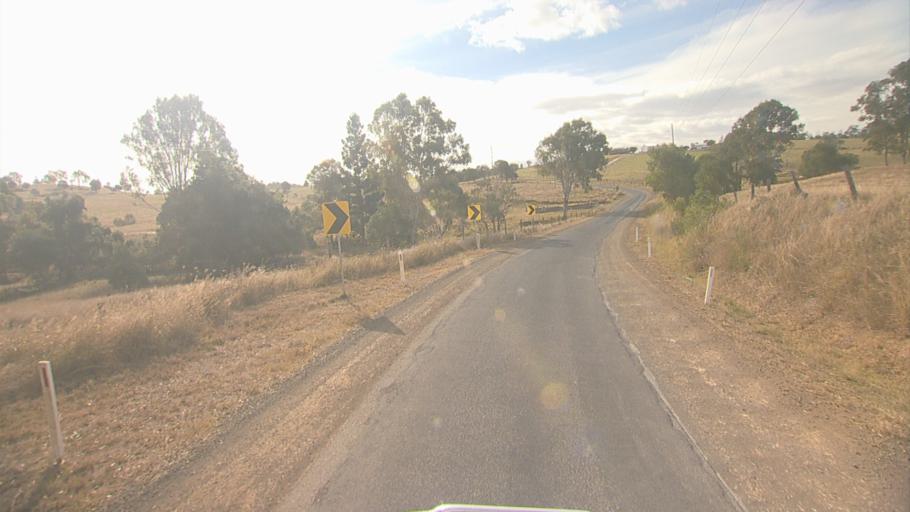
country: AU
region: Queensland
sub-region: Logan
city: Cedar Vale
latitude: -27.9131
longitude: 153.0137
